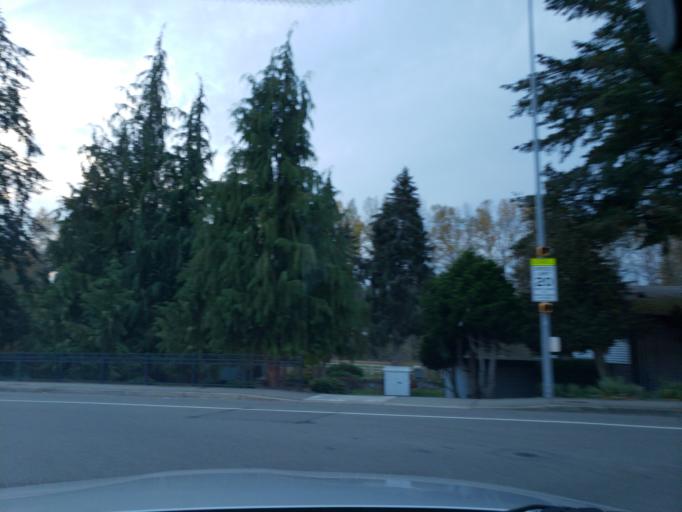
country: US
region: Washington
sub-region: King County
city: Kenmore
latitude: 47.7684
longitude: -122.2422
